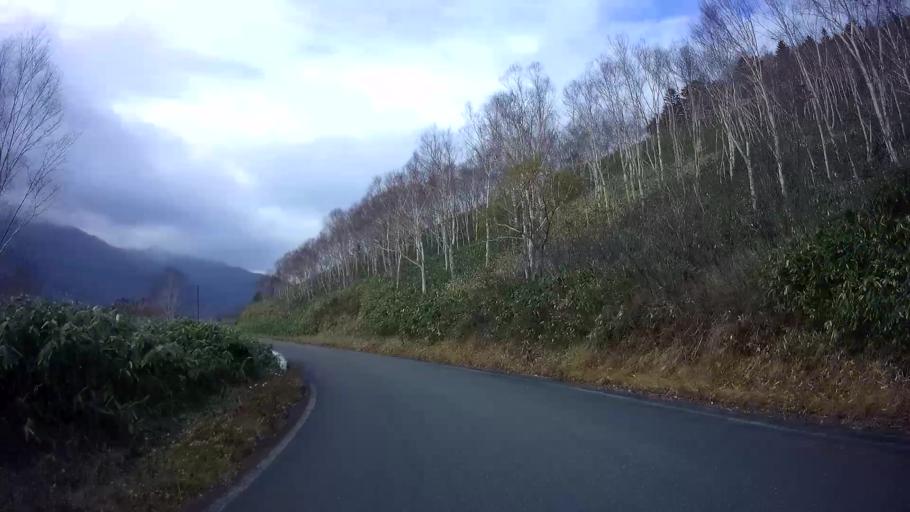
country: JP
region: Gunma
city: Nakanojomachi
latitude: 36.7046
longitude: 138.6540
